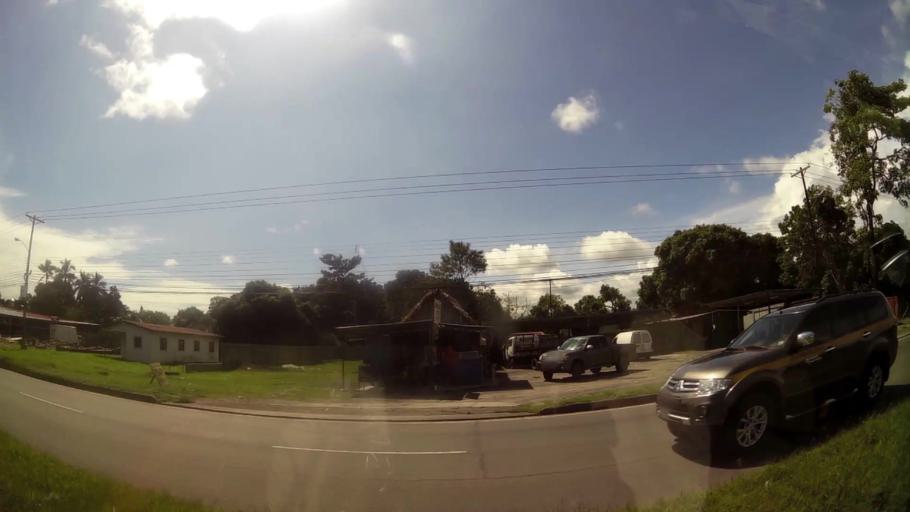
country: PA
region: Panama
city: Bejuco
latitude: 8.5937
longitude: -79.8871
